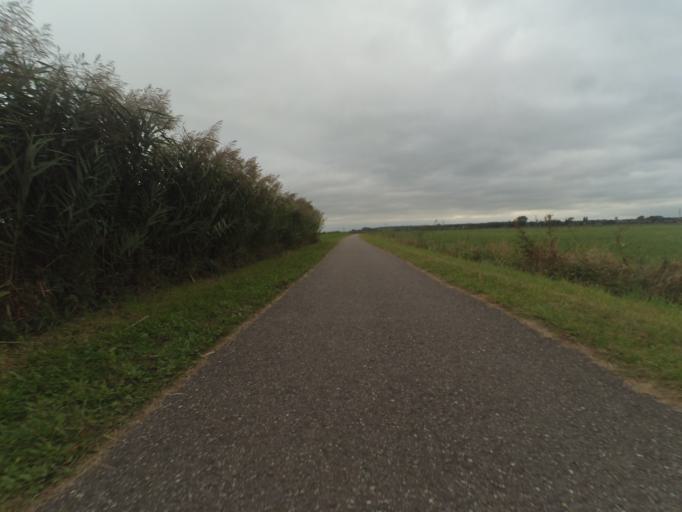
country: NL
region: Utrecht
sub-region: Gemeente Rhenen
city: Rhenen
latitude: 51.9883
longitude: 5.6140
